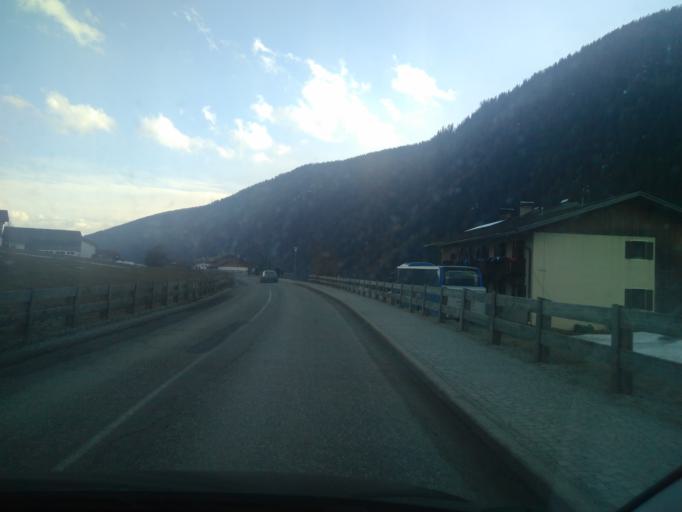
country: IT
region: Trentino-Alto Adige
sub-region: Bolzano
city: Fortezza
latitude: 46.8461
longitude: 11.6232
